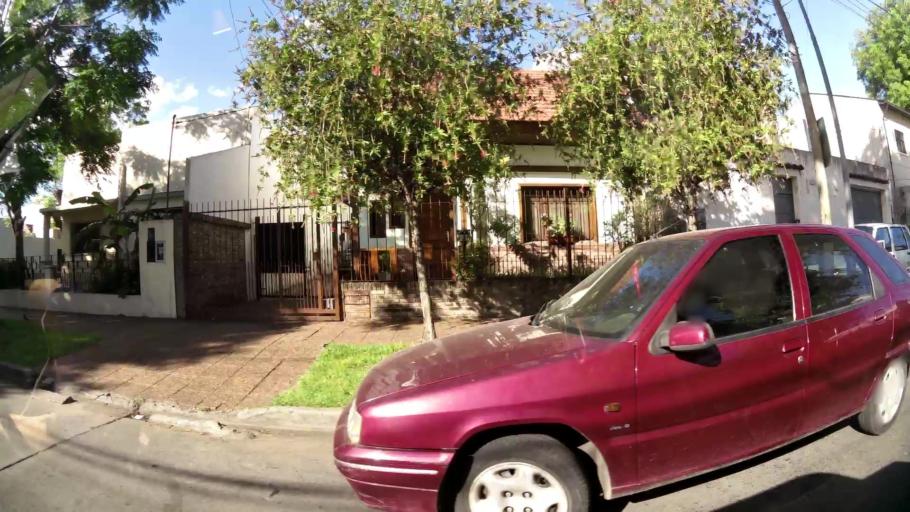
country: AR
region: Buenos Aires
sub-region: Partido de General San Martin
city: General San Martin
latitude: -34.5421
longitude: -58.5562
